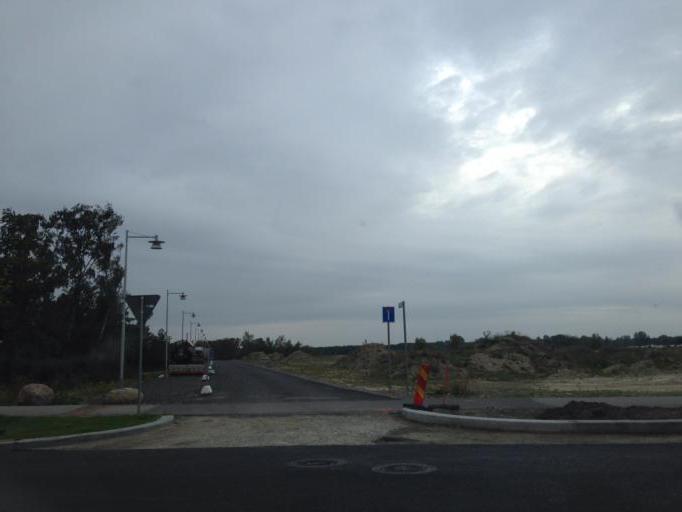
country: SE
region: Skane
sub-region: Lomma Kommun
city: Lomma
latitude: 55.6787
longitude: 13.0633
